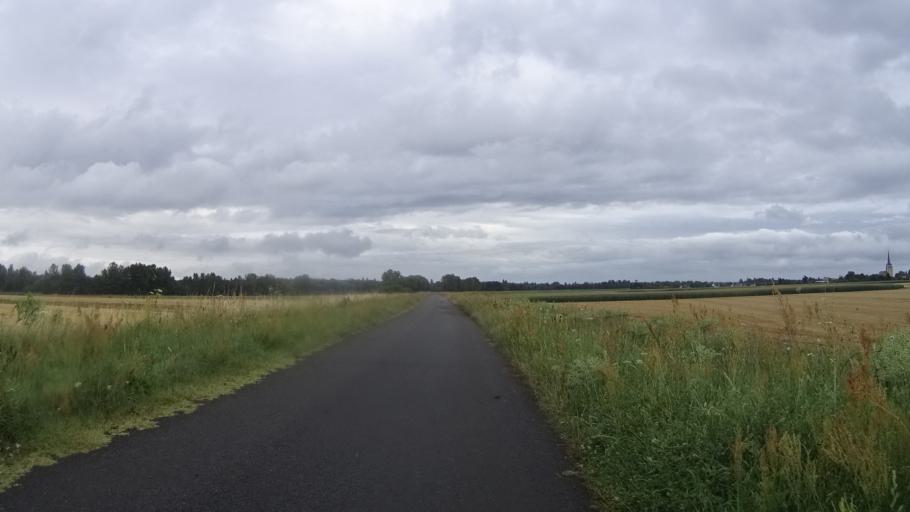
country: FR
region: Centre
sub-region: Departement du Loiret
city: Darvoy
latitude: 47.8654
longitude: 2.0850
